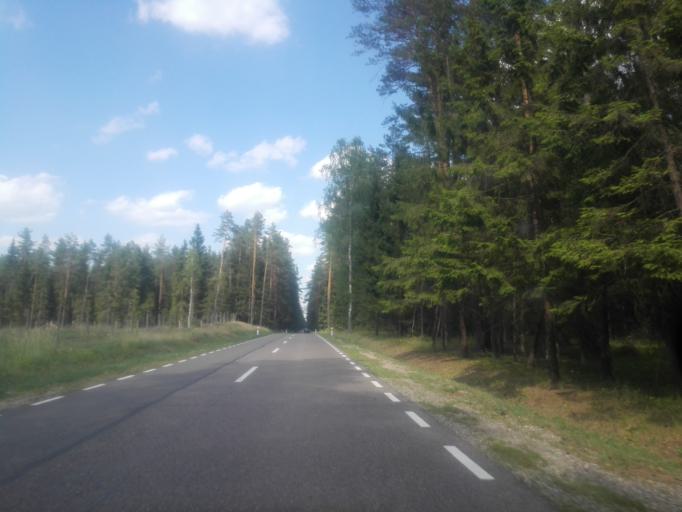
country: PL
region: Podlasie
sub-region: Powiat augustowski
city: Augustow
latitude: 53.9105
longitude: 23.1406
